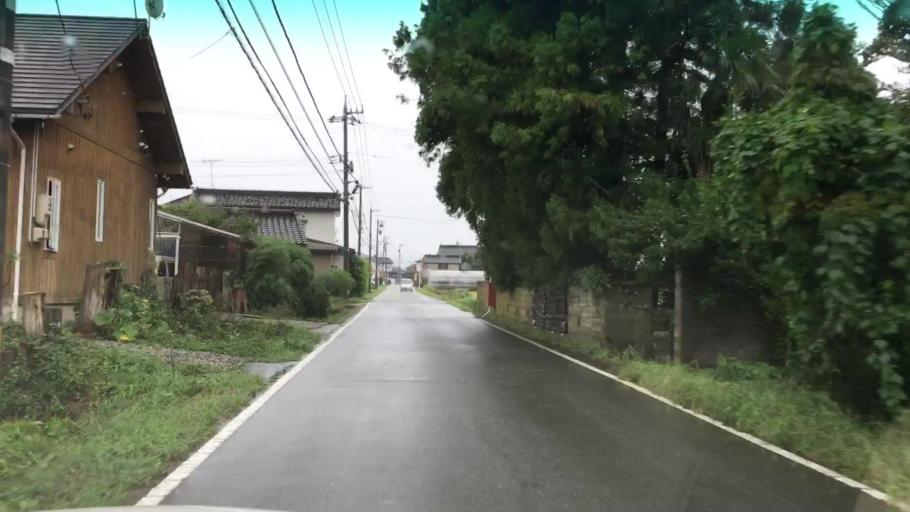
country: JP
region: Toyama
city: Kamiichi
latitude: 36.6733
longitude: 137.3207
